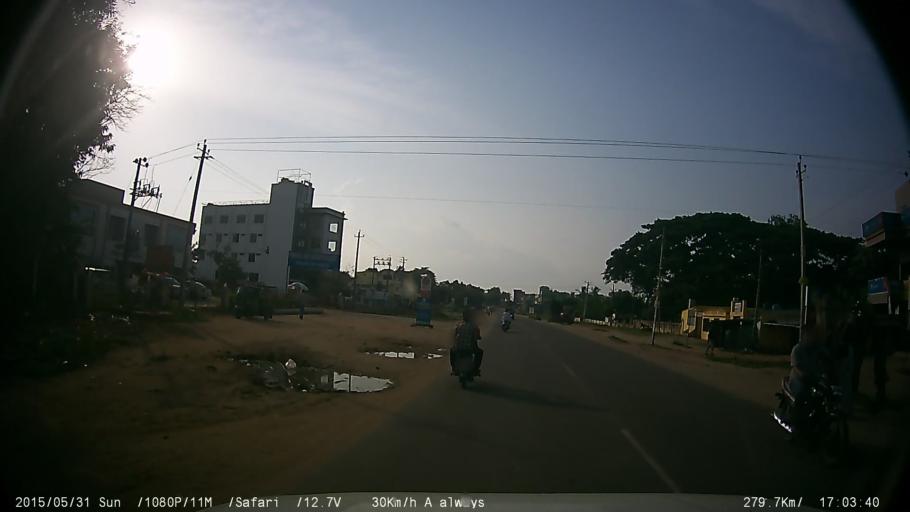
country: IN
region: Karnataka
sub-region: Chamrajnagar
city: Gundlupet
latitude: 11.8141
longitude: 76.6860
